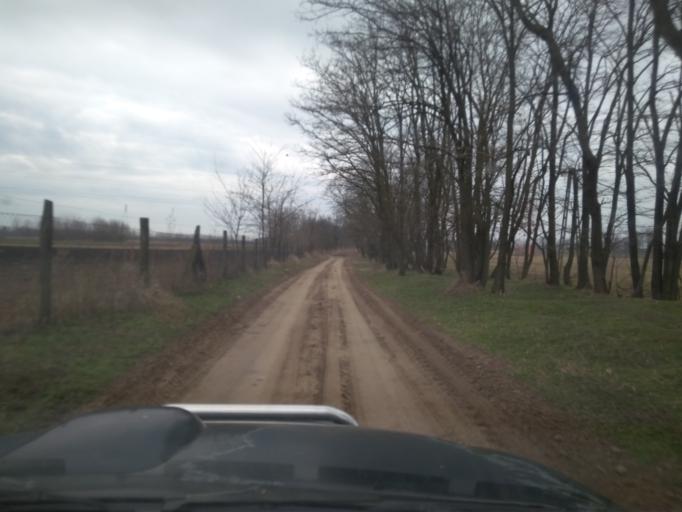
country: HU
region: Szabolcs-Szatmar-Bereg
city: Nyiregyhaza
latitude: 47.9655
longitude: 21.6685
